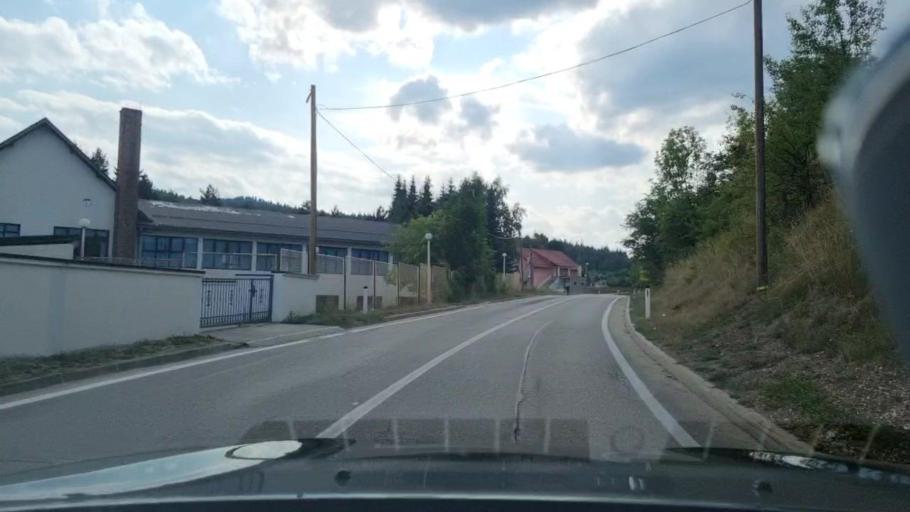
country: BA
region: Federation of Bosnia and Herzegovina
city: Glamoc
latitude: 44.0486
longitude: 16.8459
